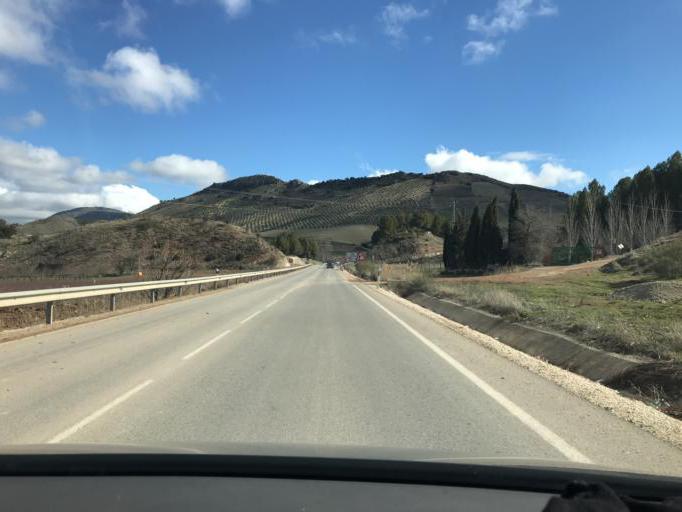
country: ES
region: Andalusia
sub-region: Provincia de Jaen
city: Huelma
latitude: 37.6490
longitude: -3.4257
